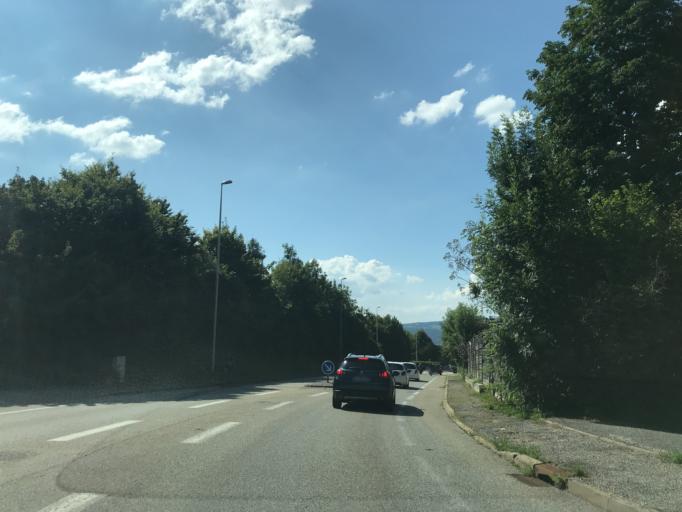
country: FR
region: Rhone-Alpes
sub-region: Departement de la Haute-Savoie
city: Villaz
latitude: 45.9214
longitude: 6.1777
